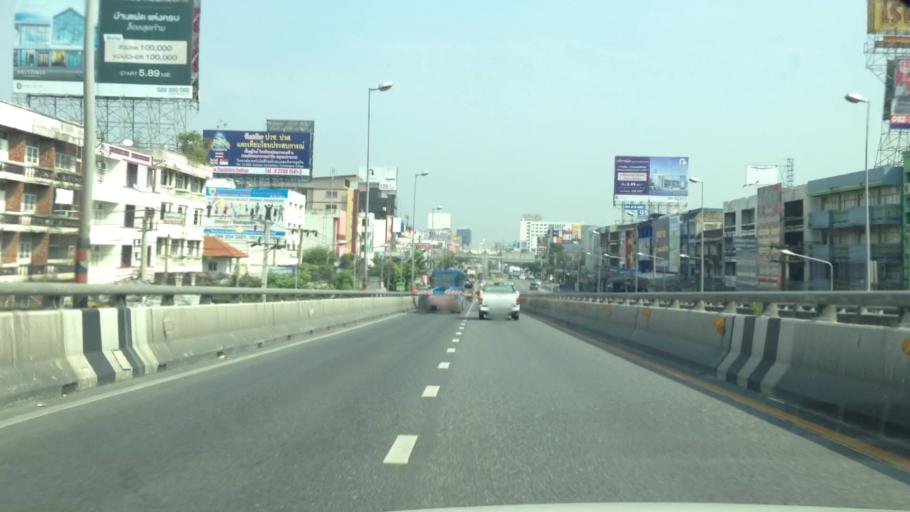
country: TH
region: Bangkok
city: Bang Na
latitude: 13.6310
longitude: 100.6287
